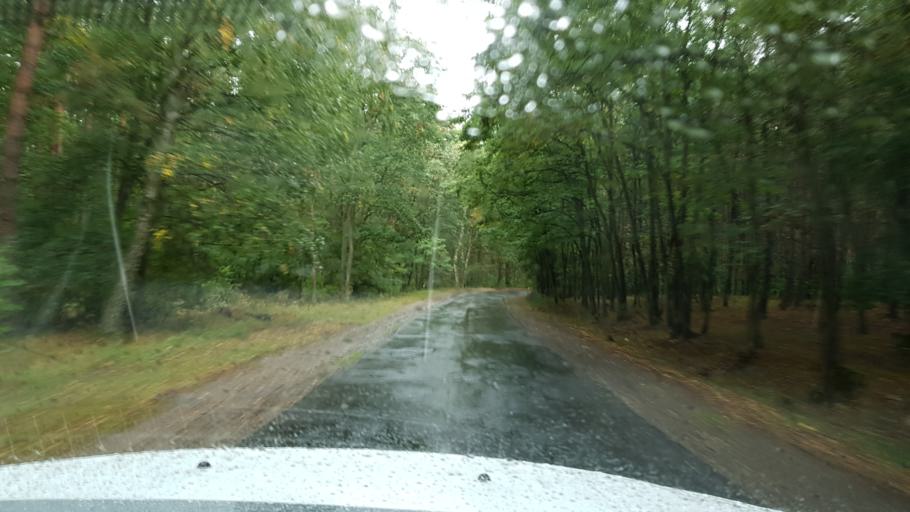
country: DE
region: Brandenburg
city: Meyenburg
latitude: 52.9738
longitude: 14.2350
